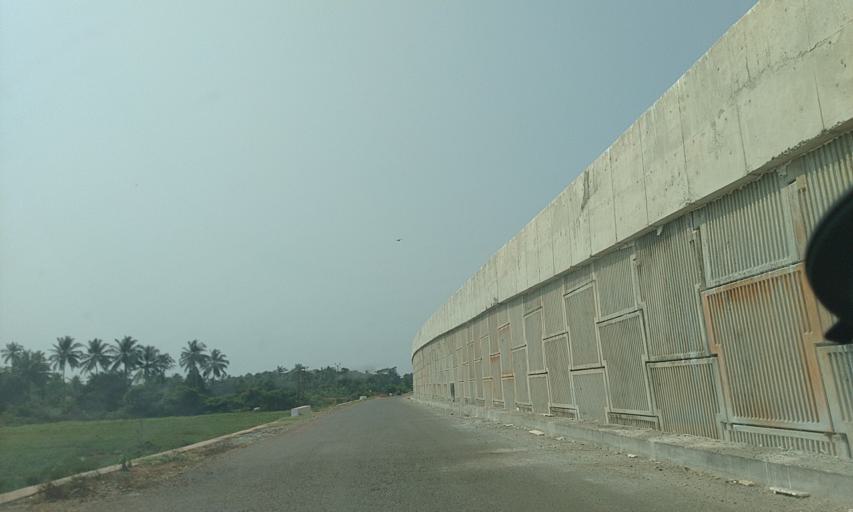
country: IN
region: Goa
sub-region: South Goa
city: Raia
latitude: 15.3059
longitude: 73.9449
